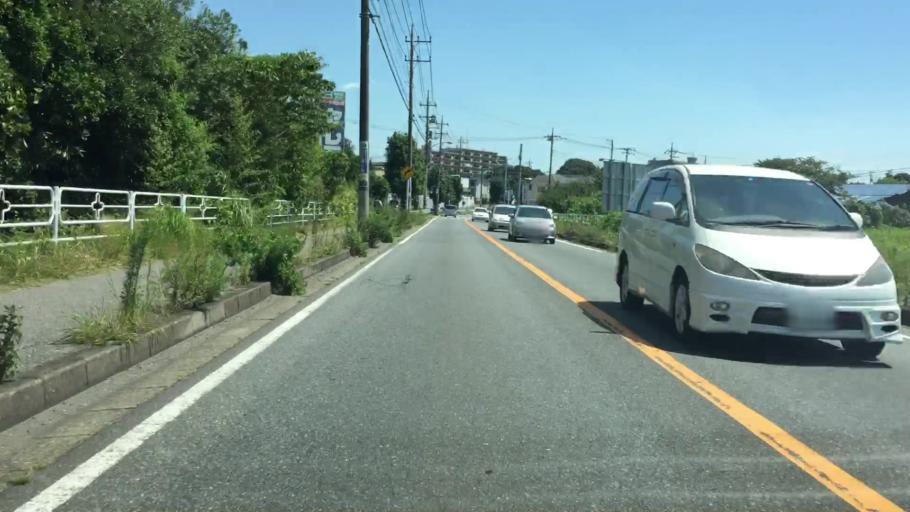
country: JP
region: Chiba
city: Funabashi
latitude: 35.7361
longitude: 139.9563
